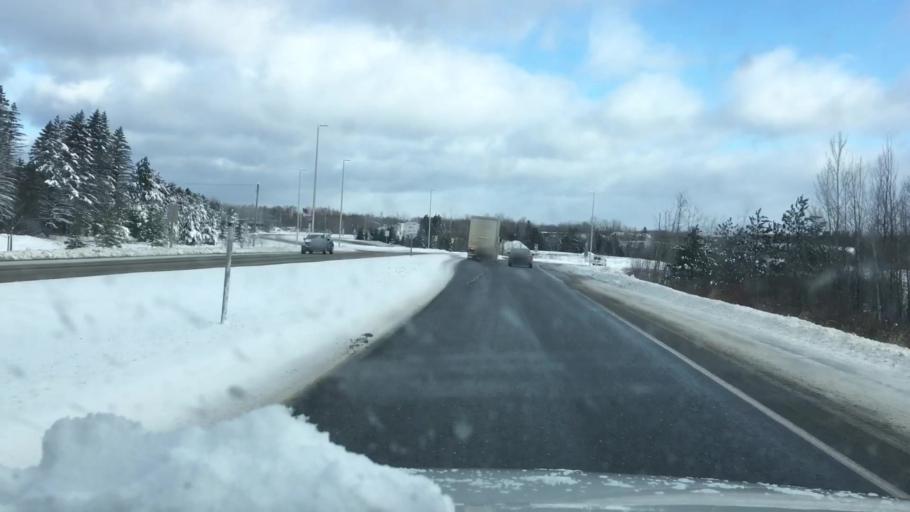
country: US
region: Maine
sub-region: Aroostook County
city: Caribou
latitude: 46.8664
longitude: -67.9993
